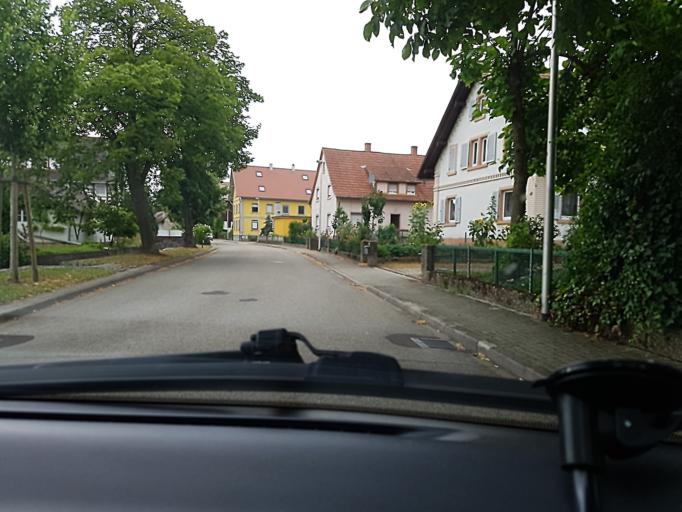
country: DE
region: Baden-Wuerttemberg
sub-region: Freiburg Region
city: Willstatt
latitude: 48.5557
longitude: 7.8841
